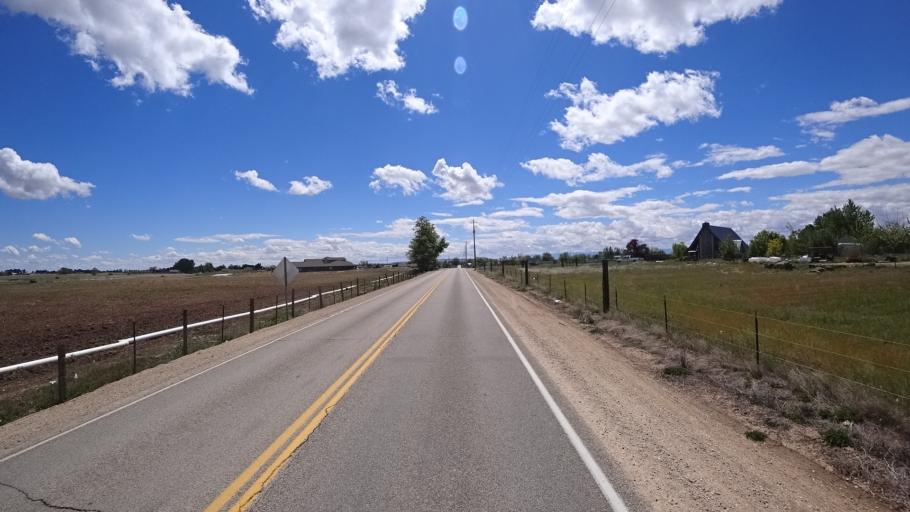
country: US
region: Idaho
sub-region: Ada County
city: Kuna
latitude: 43.5598
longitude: -116.4537
